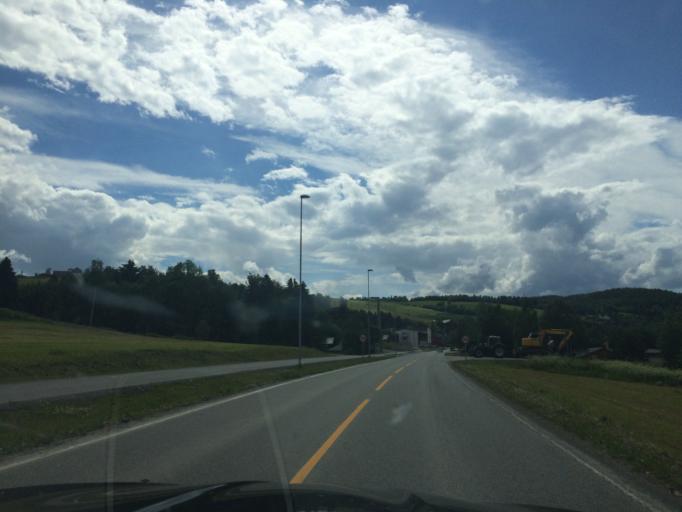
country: NO
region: Sor-Trondelag
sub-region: Selbu
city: Mebonden
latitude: 63.2448
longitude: 11.0903
